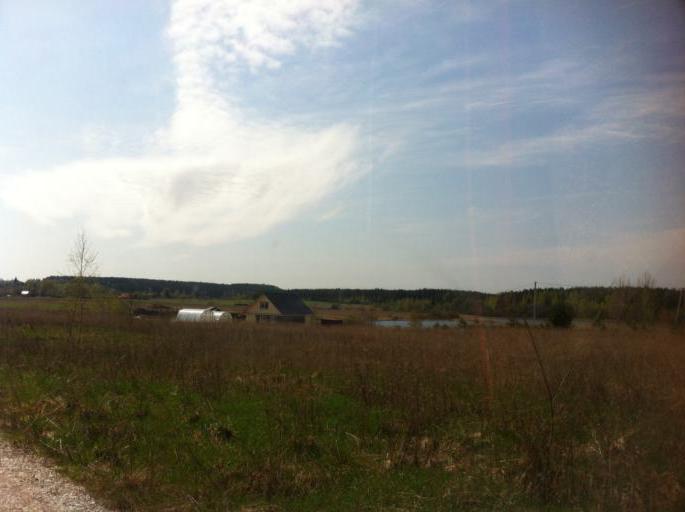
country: RU
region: Pskov
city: Izborsk
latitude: 57.8254
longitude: 27.9658
